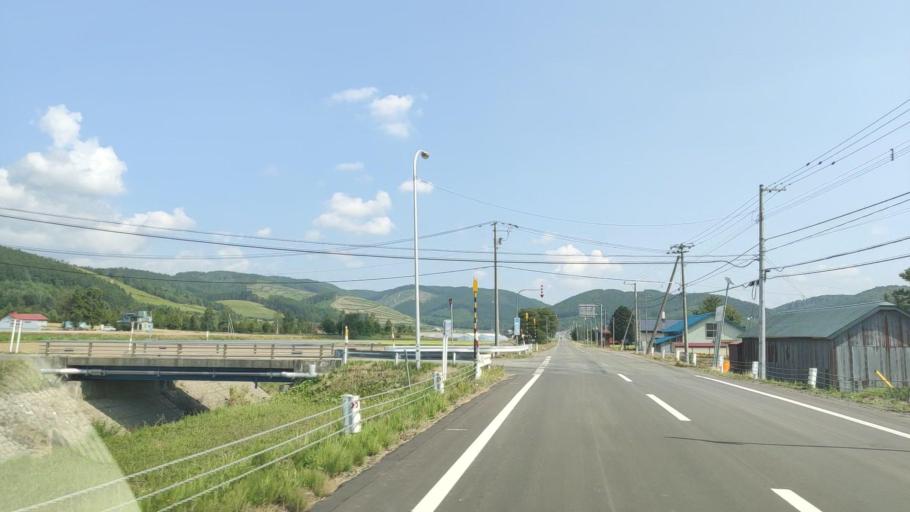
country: JP
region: Hokkaido
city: Shimo-furano
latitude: 43.4058
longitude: 142.3957
